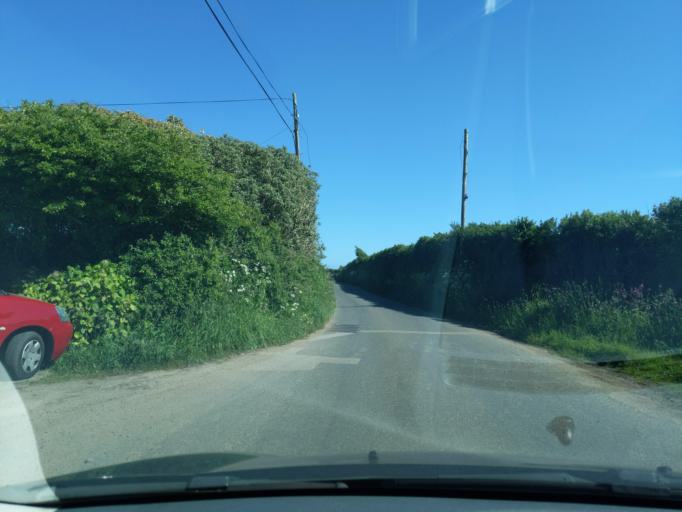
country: GB
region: England
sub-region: Cornwall
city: St. Buryan
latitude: 50.0704
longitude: -5.6114
